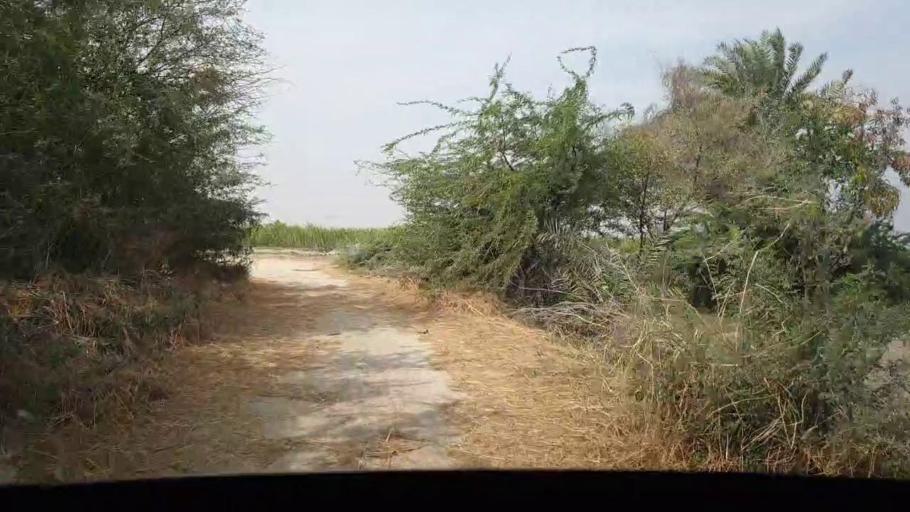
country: PK
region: Sindh
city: Chuhar Jamali
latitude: 24.3213
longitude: 67.9517
